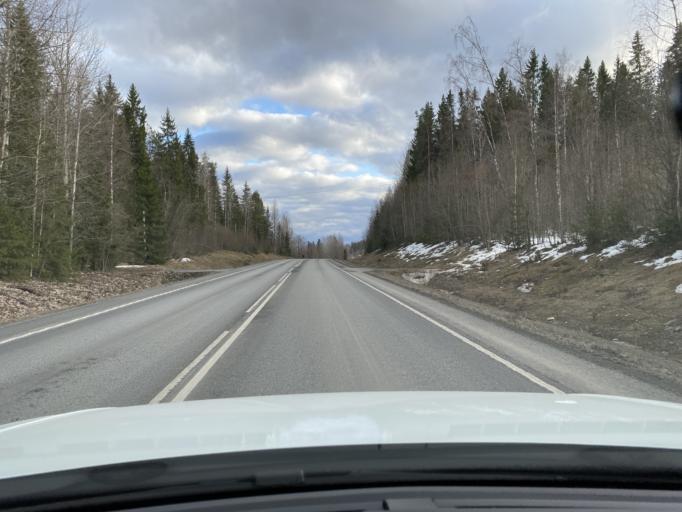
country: FI
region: Pirkanmaa
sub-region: Lounais-Pirkanmaa
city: Mouhijaervi
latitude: 61.4291
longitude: 23.0041
